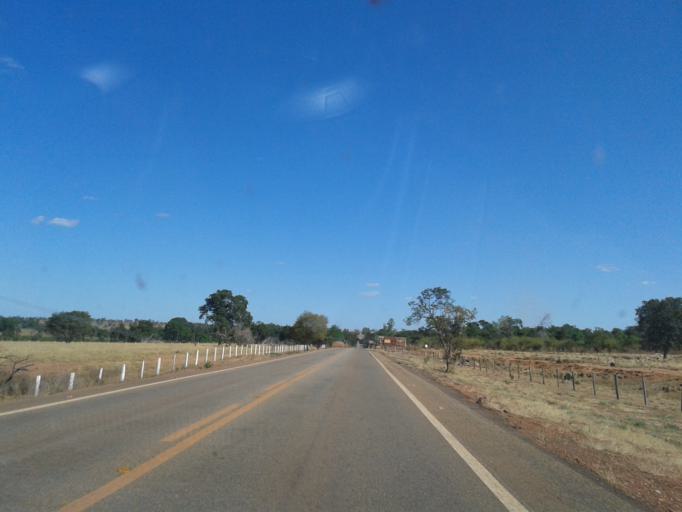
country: BR
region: Goias
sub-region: Crixas
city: Crixas
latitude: -14.2138
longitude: -50.3916
